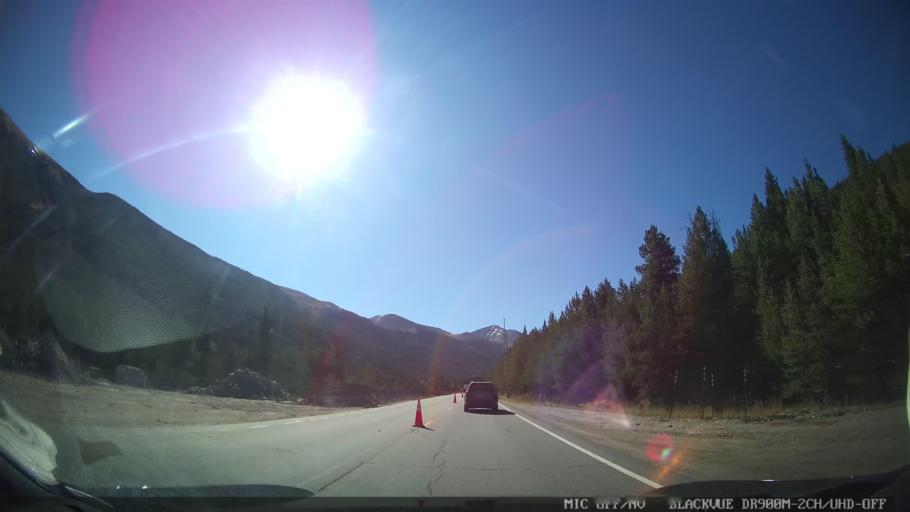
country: US
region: Colorado
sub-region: Summit County
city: Frisco
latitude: 39.4928
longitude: -106.1361
